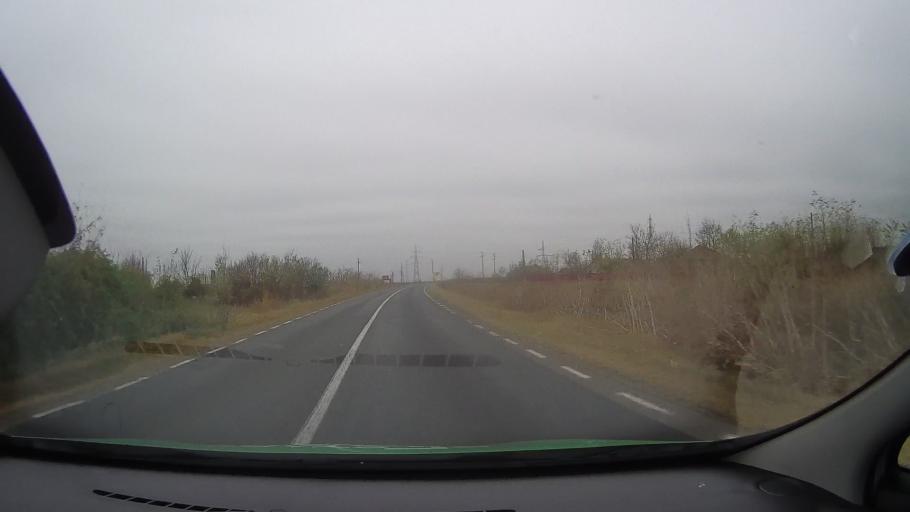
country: RO
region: Braila
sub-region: Comuna Baraganul
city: Baraganul
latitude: 44.7968
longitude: 27.5123
